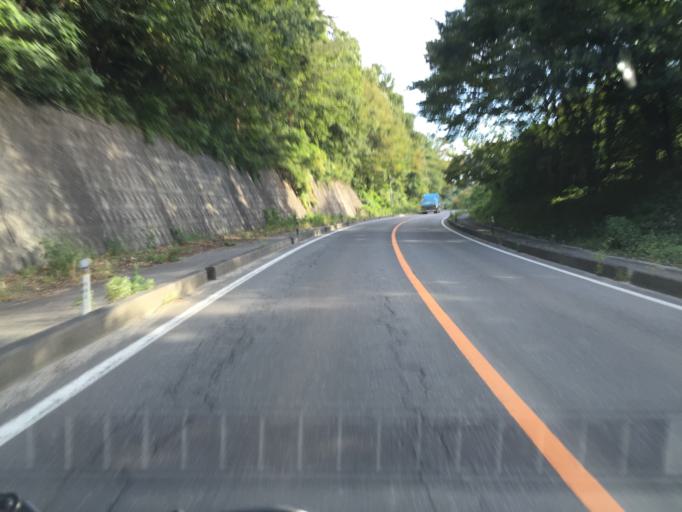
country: JP
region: Fukushima
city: Hobaramachi
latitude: 37.7608
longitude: 140.5974
